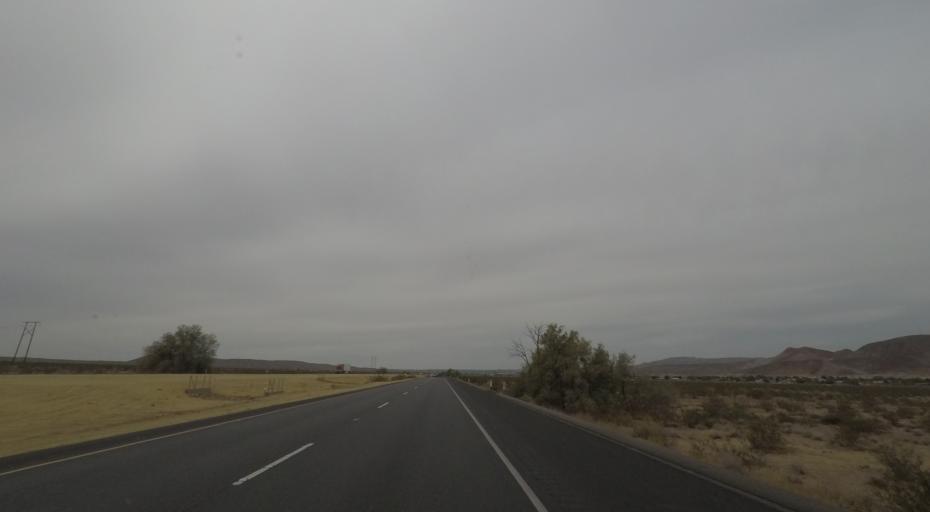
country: US
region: California
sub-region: San Bernardino County
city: Barstow
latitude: 34.8518
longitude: -116.8732
